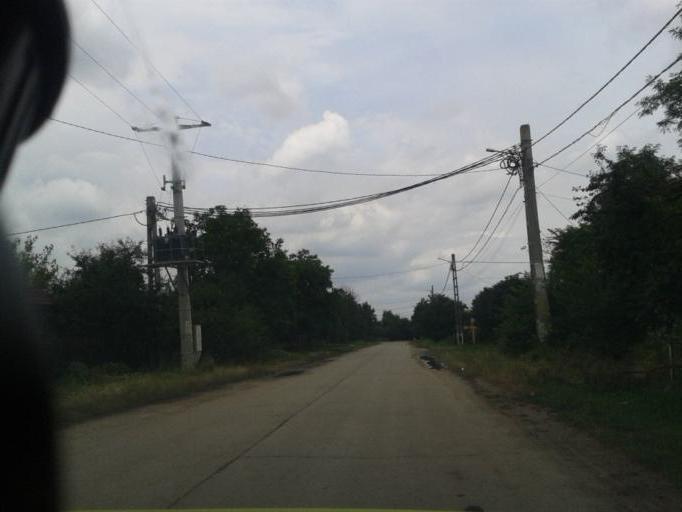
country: RO
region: Ialomita
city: Dragoesti-Snagov
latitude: 44.5300
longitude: 26.4820
